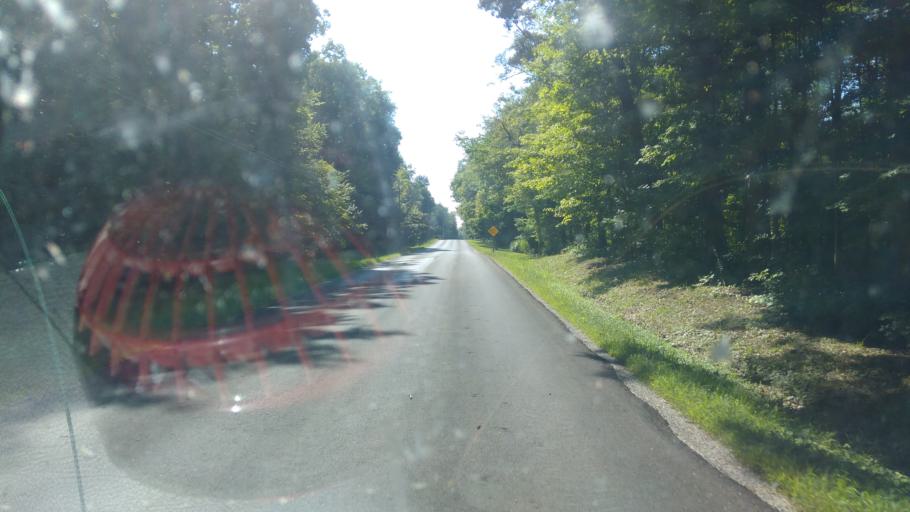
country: US
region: Ohio
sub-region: Ashland County
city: Ashland
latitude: 40.9698
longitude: -82.2925
